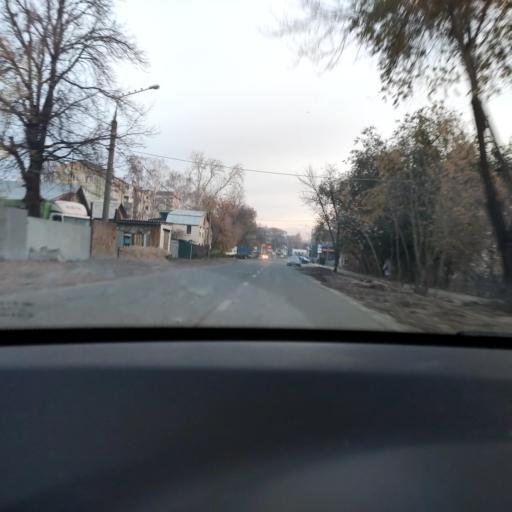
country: RU
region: Samara
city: Samara
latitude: 53.1989
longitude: 50.1985
